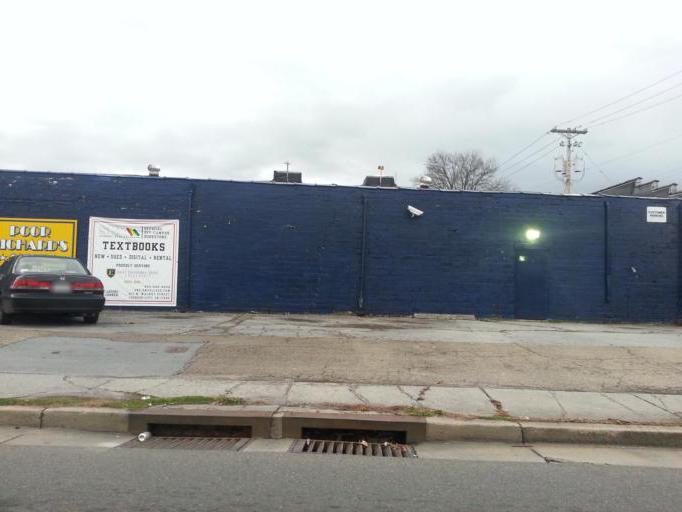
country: US
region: Tennessee
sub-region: Washington County
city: Johnson City
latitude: 36.3070
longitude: -82.3644
